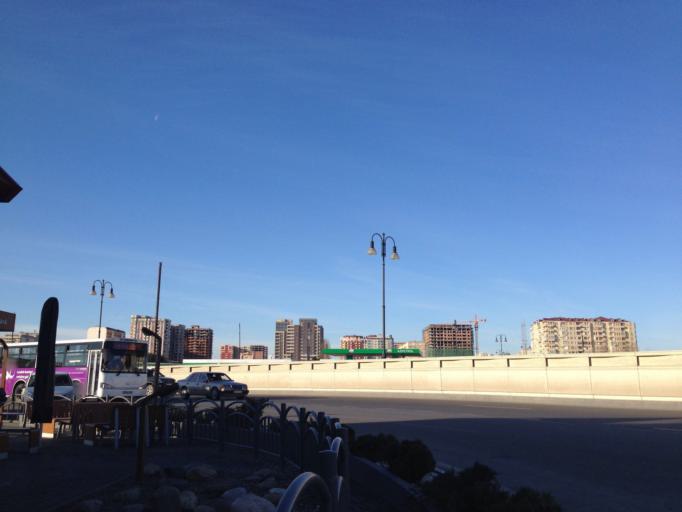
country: AZ
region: Baki
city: Baku
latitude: 40.3997
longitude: 49.8498
